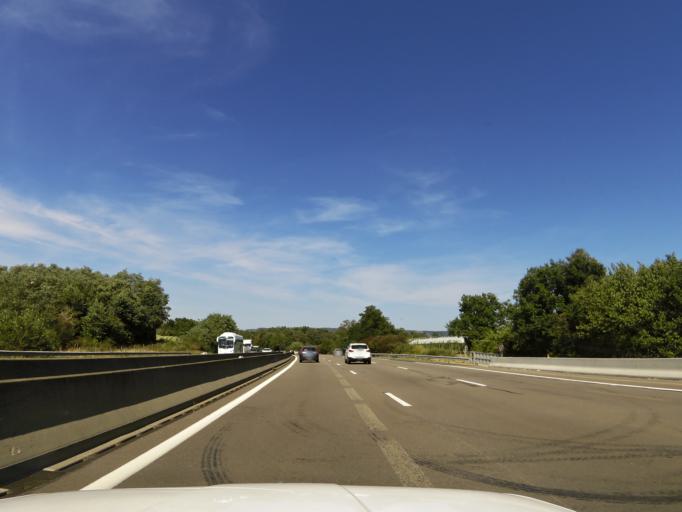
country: FR
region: Rhone-Alpes
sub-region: Departement de l'Isere
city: Auberives-sur-Vareze
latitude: 45.4148
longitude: 4.8267
